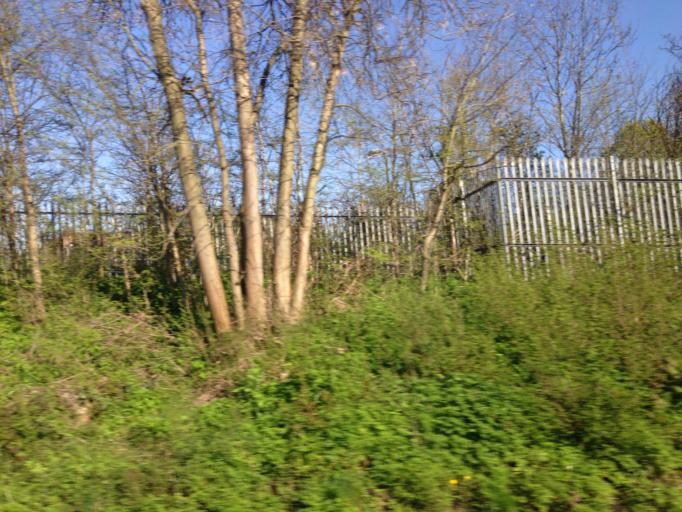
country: GB
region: England
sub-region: Greater London
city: Mitcham
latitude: 51.4033
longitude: -0.1573
